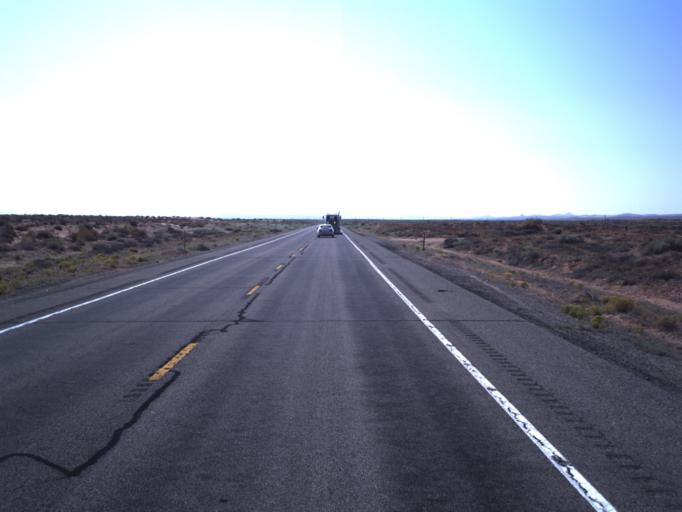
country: US
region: Utah
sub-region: San Juan County
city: Blanding
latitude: 37.2158
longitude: -109.6132
